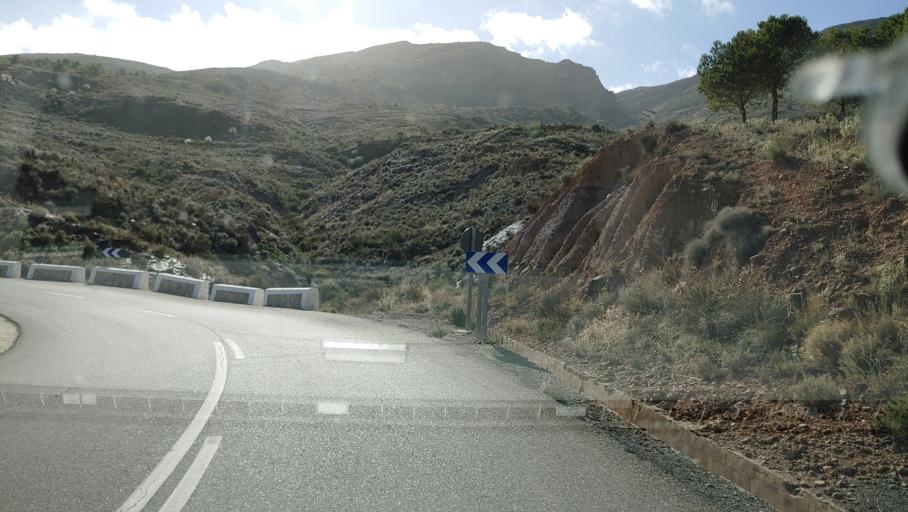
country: ES
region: Andalusia
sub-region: Provincia de Almeria
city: Alicun
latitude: 36.9365
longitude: -2.6062
